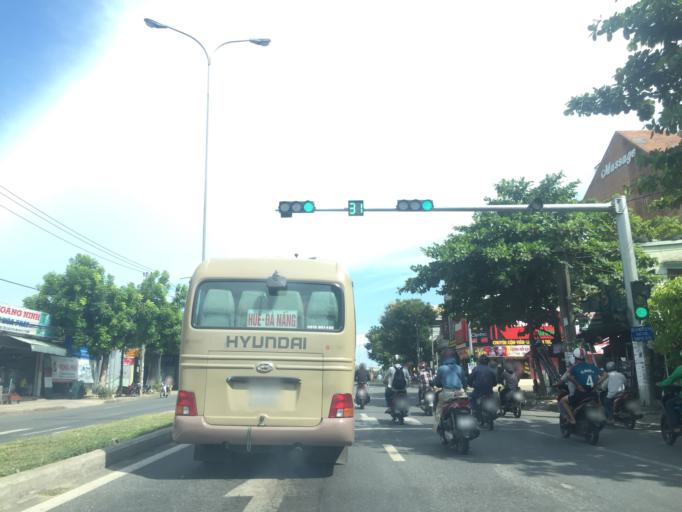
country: VN
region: Da Nang
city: Lien Chieu
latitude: 16.0591
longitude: 108.1643
